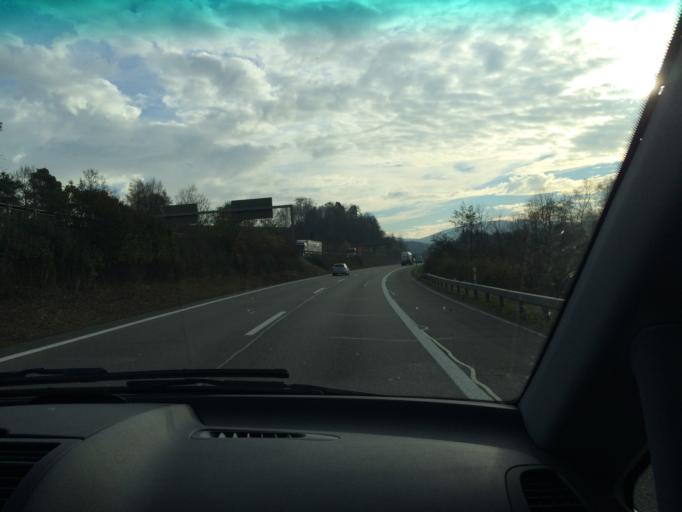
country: CH
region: Aargau
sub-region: Bezirk Rheinfelden
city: Kaiseraugst
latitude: 47.5296
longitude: 7.7354
